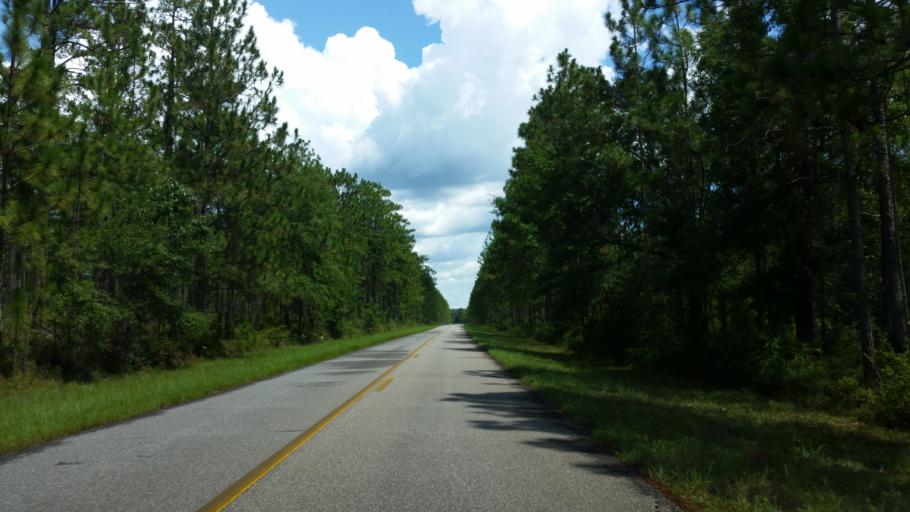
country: US
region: Florida
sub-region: Santa Rosa County
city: East Milton
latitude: 30.7409
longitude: -86.8240
